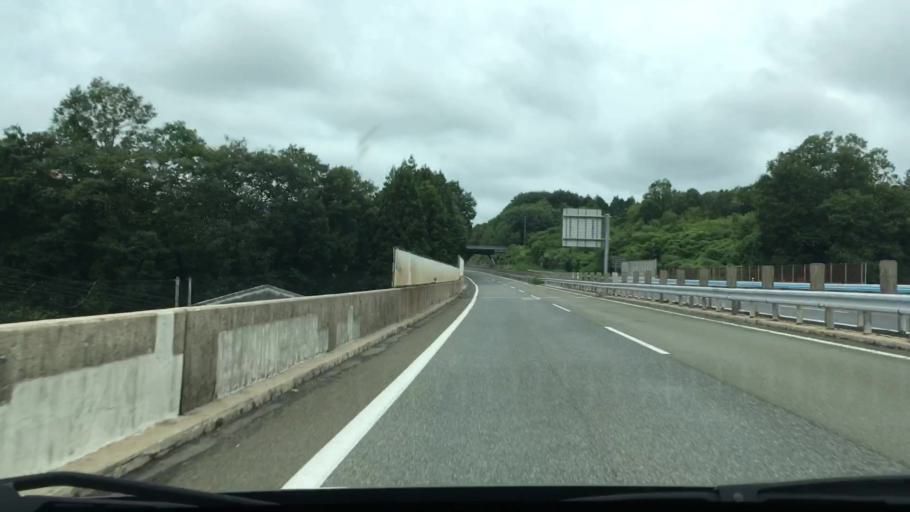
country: JP
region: Hiroshima
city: Miyoshi
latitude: 34.7955
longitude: 132.8883
